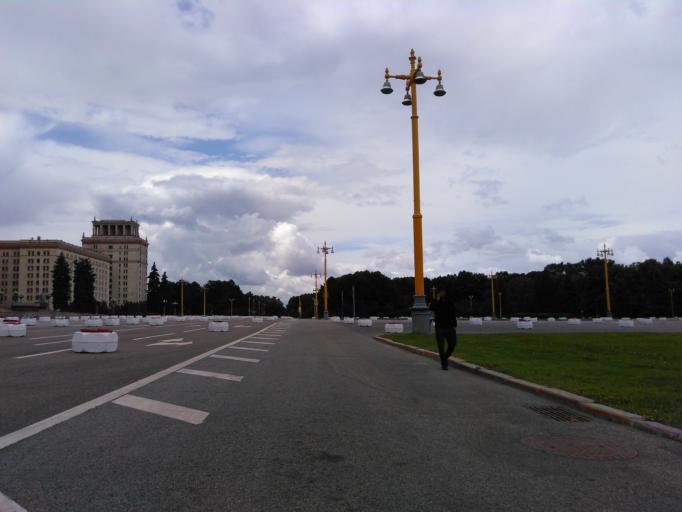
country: RU
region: Moscow
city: Vorob'yovo
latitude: 55.7034
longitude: 37.5343
